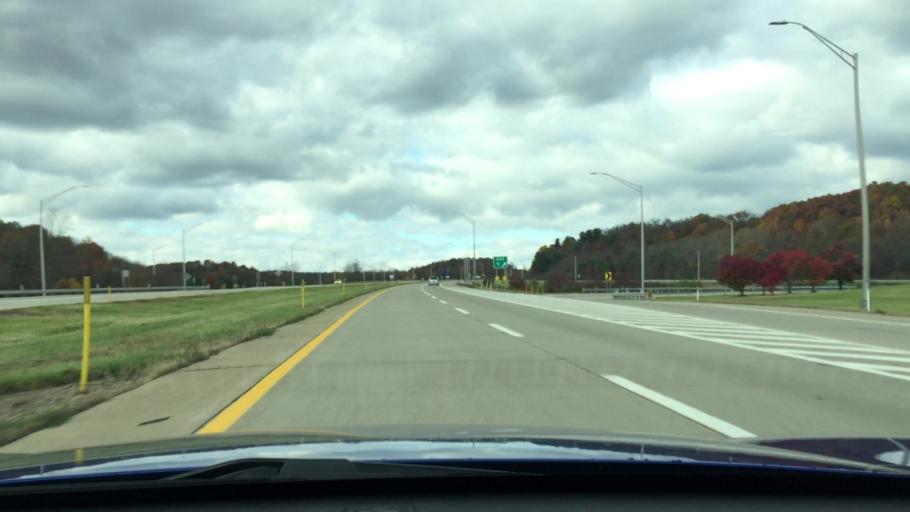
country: US
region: Pennsylvania
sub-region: Westmoreland County
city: New Stanton
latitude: 40.2334
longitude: -79.6016
